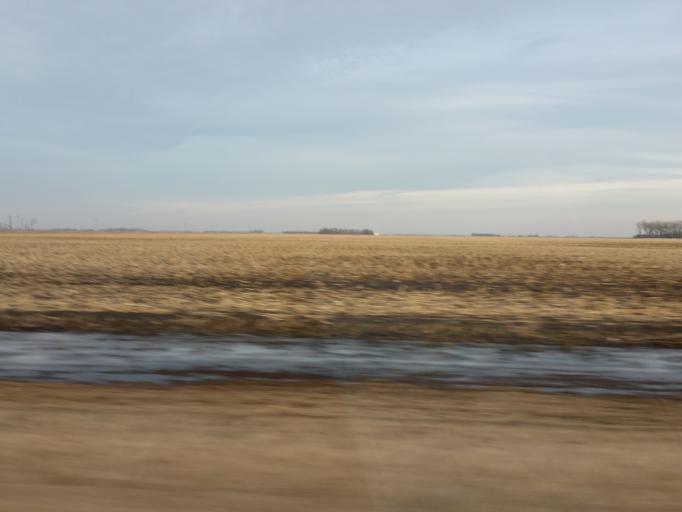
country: US
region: North Dakota
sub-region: Traill County
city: Mayville
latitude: 47.4230
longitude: -97.3260
